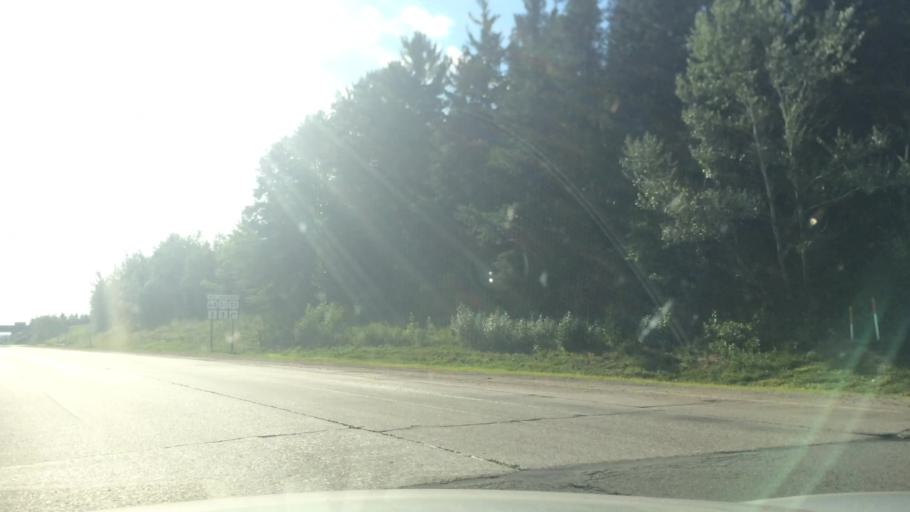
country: US
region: Wisconsin
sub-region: Lincoln County
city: Merrill
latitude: 45.1778
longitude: -89.6418
